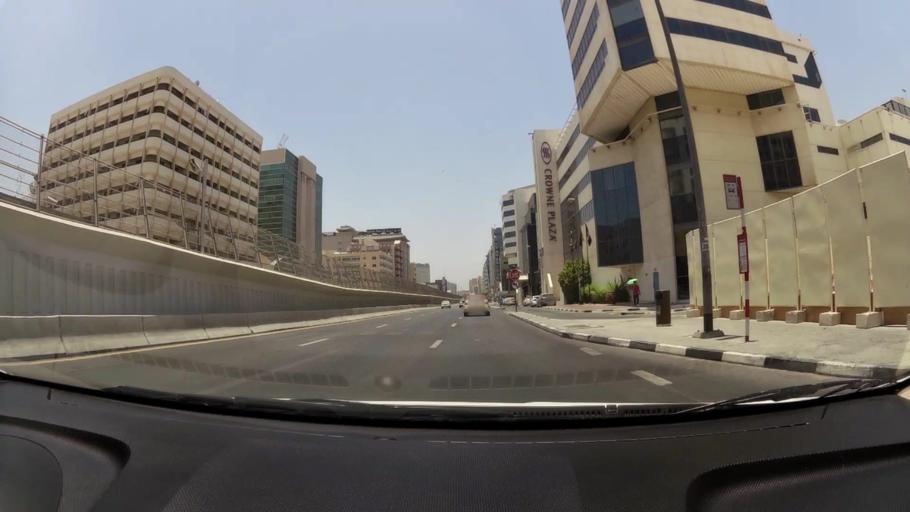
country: AE
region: Ash Shariqah
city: Sharjah
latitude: 25.2703
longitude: 55.3280
